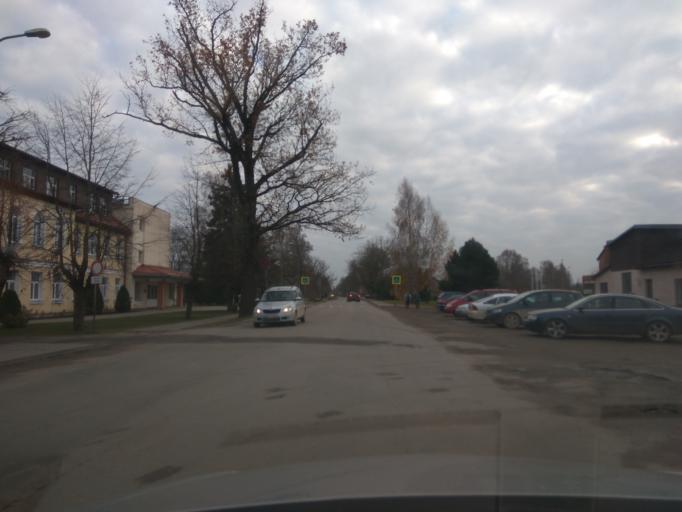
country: LV
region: Kuldigas Rajons
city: Kuldiga
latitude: 56.9628
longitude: 21.9822
